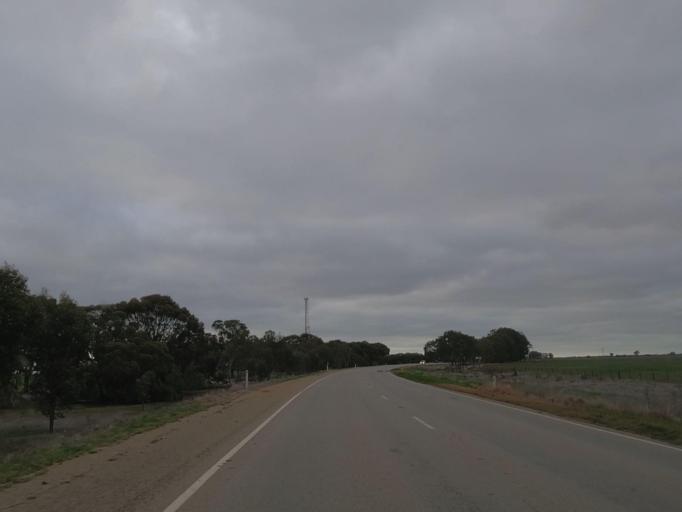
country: AU
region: Victoria
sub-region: Swan Hill
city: Swan Hill
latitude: -35.9264
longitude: 143.9360
